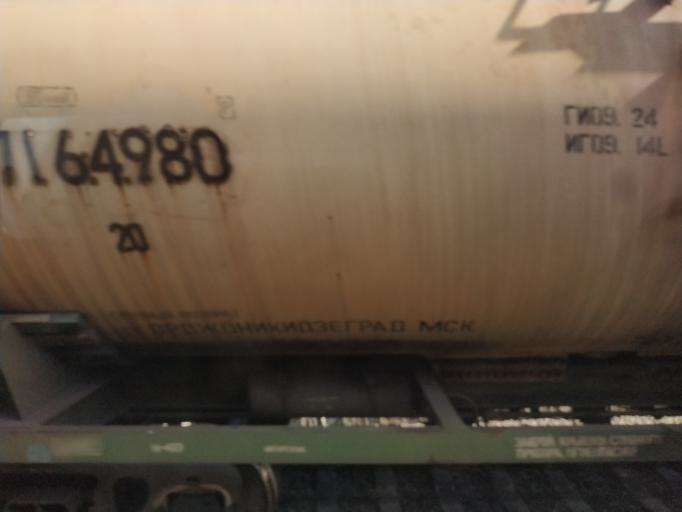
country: RU
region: Volgograd
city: Gumrak
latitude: 48.7804
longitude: 44.3769
